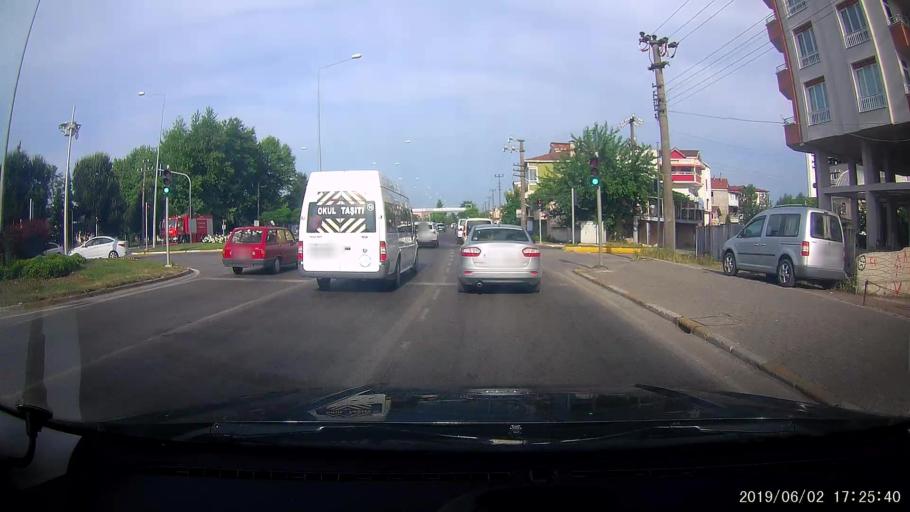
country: TR
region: Samsun
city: Carsamba
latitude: 41.2047
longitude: 36.7103
